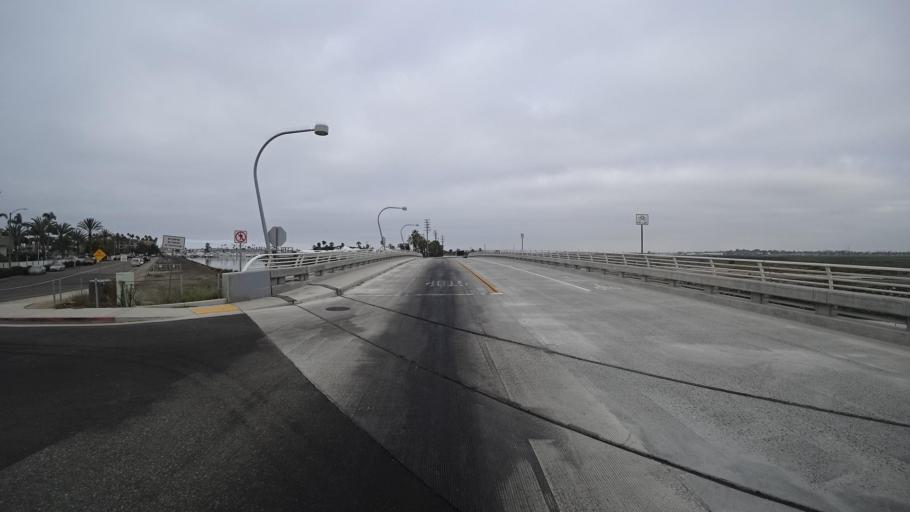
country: US
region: California
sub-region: Orange County
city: Seal Beach
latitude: 33.7296
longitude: -118.0695
